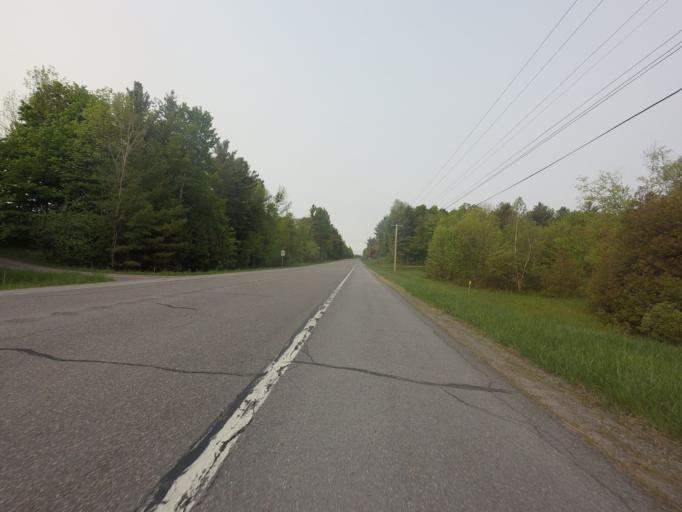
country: US
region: New York
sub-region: St. Lawrence County
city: Gouverneur
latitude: 44.1150
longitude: -75.3951
